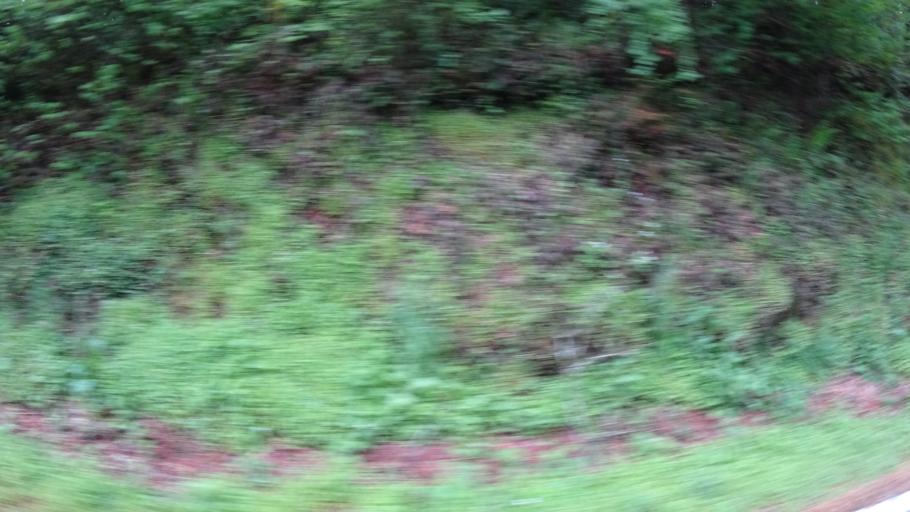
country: US
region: Oregon
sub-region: Washington County
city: West Haven-Sylvan
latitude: 45.5391
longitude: -122.7402
